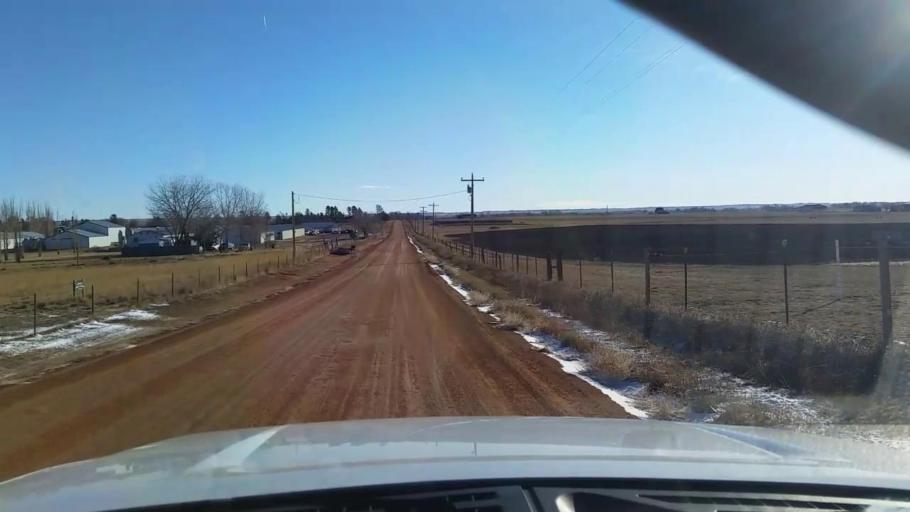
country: US
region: Colorado
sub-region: Larimer County
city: Wellington
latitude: 40.7695
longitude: -105.0732
